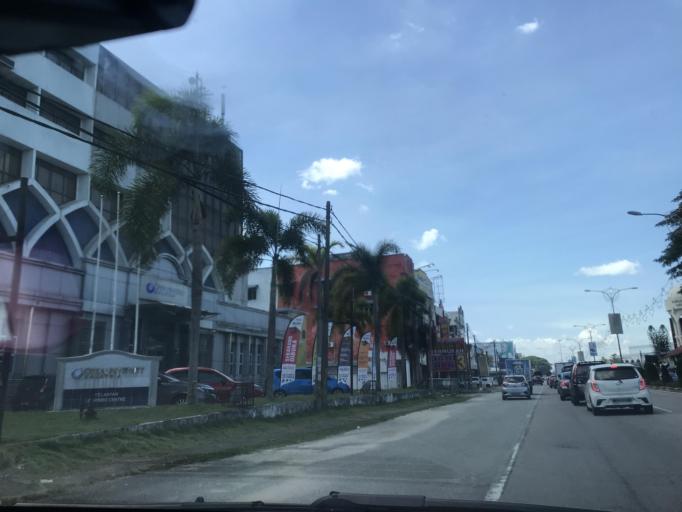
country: MY
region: Kelantan
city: Kota Bharu
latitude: 6.1046
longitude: 102.2609
